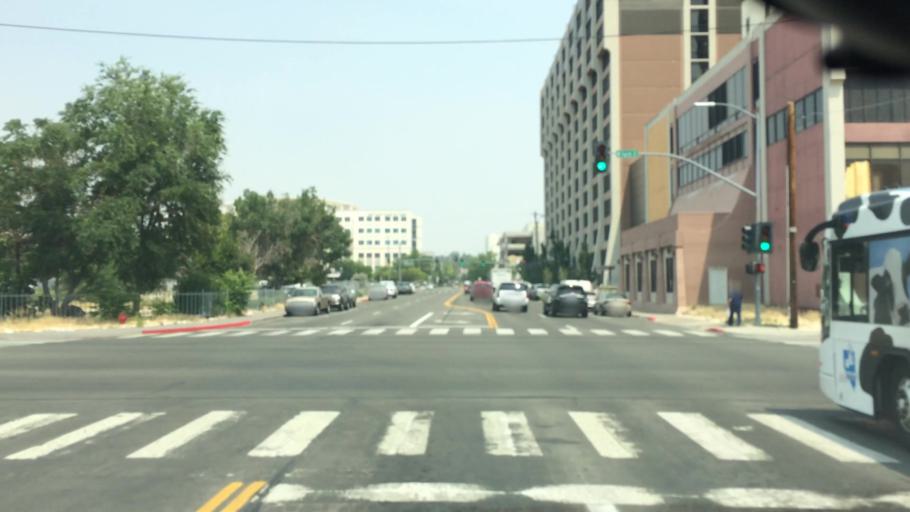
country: US
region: Nevada
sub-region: Washoe County
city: Reno
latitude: 39.5290
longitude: -119.8181
